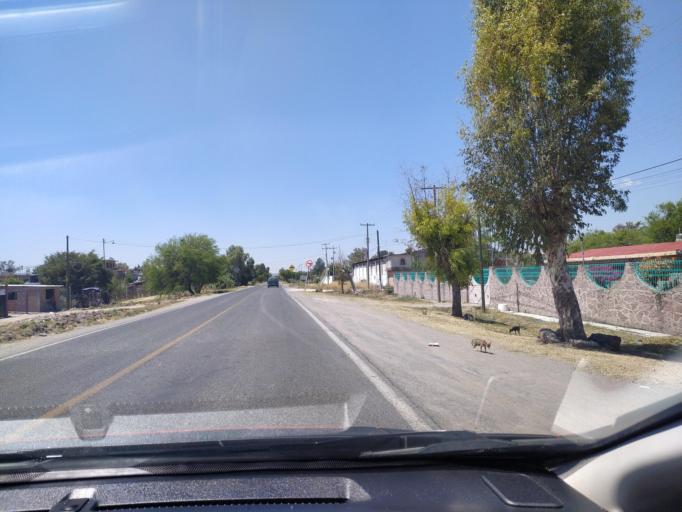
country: MX
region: Guanajuato
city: Ciudad Manuel Doblado
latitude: 20.7410
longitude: -101.8841
